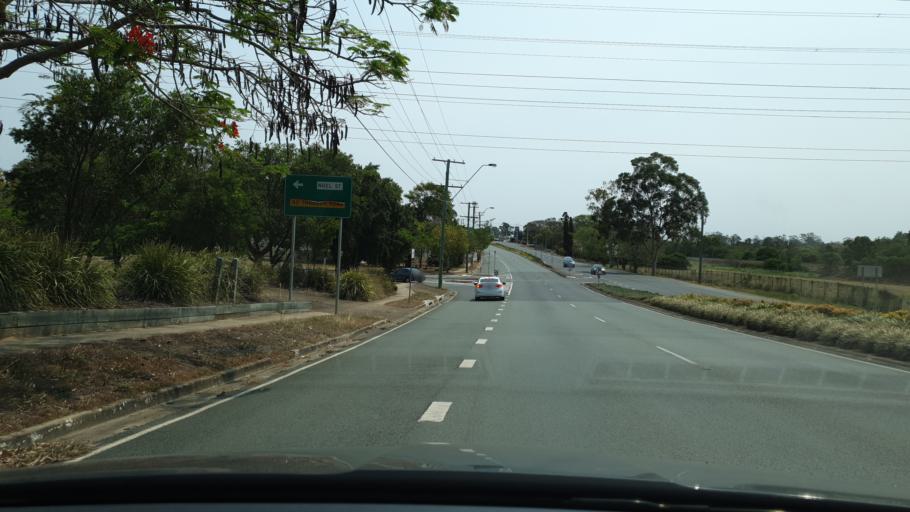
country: AU
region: Queensland
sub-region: Ipswich
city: Bundamba
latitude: -27.5995
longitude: 152.8293
